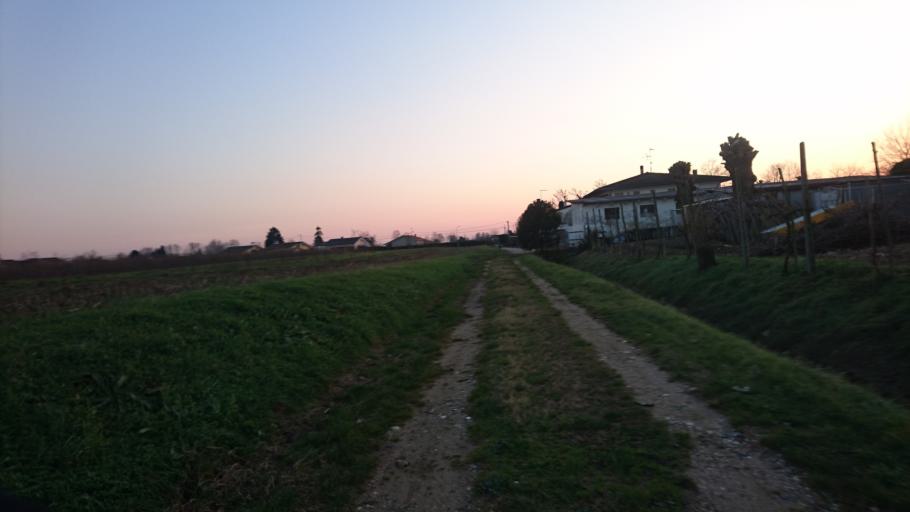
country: IT
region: Veneto
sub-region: Provincia di Padova
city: Villatora
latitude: 45.3733
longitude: 11.9589
